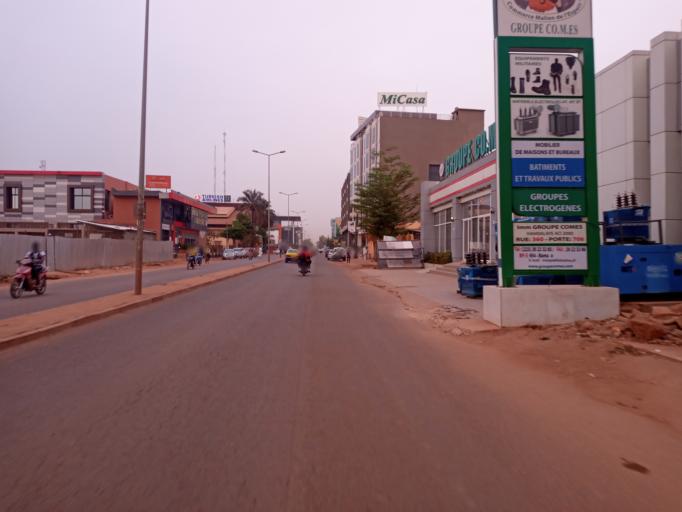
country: ML
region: Bamako
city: Bamako
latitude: 12.6358
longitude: -8.0246
